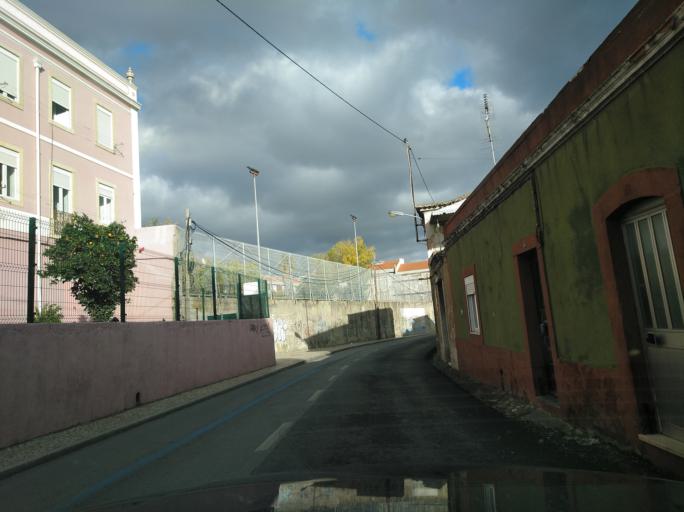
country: PT
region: Lisbon
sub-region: Loures
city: Sacavem
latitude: 38.7914
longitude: -9.1120
